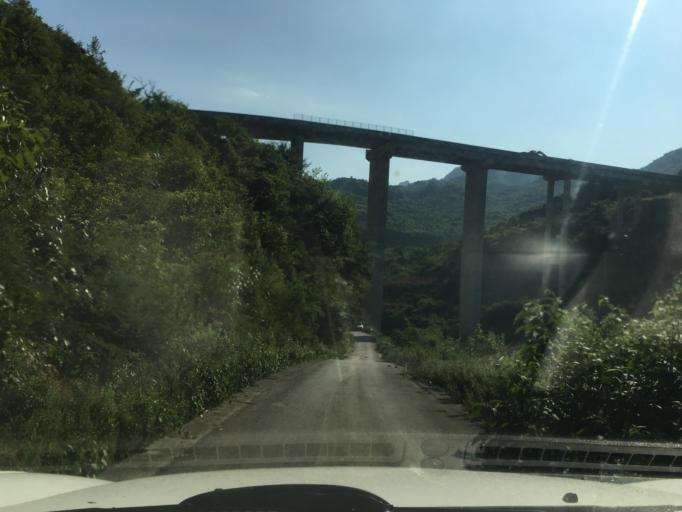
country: CN
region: Guangxi Zhuangzu Zizhiqu
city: Xinzhou
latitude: 25.4562
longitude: 105.7359
